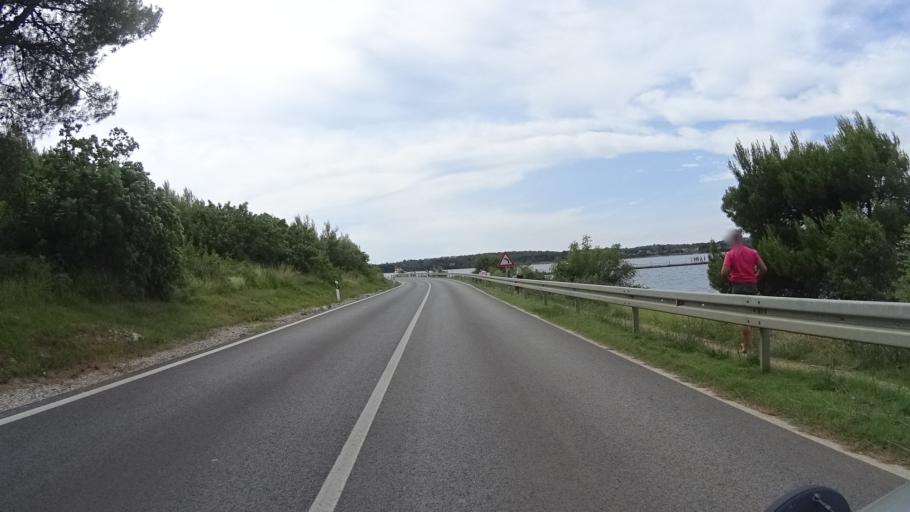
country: HR
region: Istarska
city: Medulin
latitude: 44.8167
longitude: 13.8974
